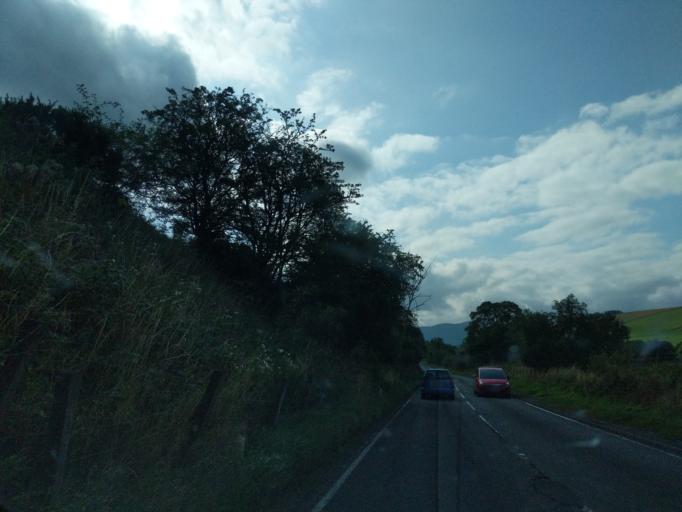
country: GB
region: Scotland
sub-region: The Scottish Borders
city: Peebles
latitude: 55.6802
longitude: -3.2062
